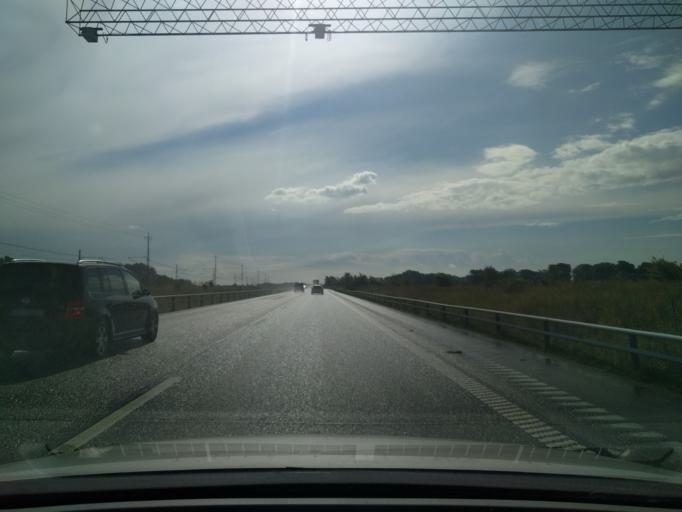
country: SE
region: Skane
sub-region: Malmo
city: Bunkeflostrand
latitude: 55.5561
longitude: 12.9430
